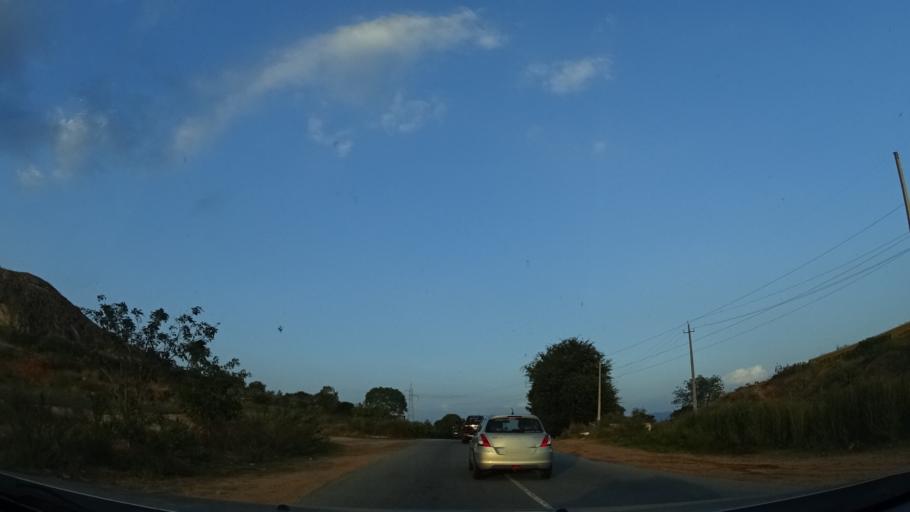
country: IN
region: Karnataka
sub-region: Ramanagara
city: Kanakapura
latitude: 12.5011
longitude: 77.3855
